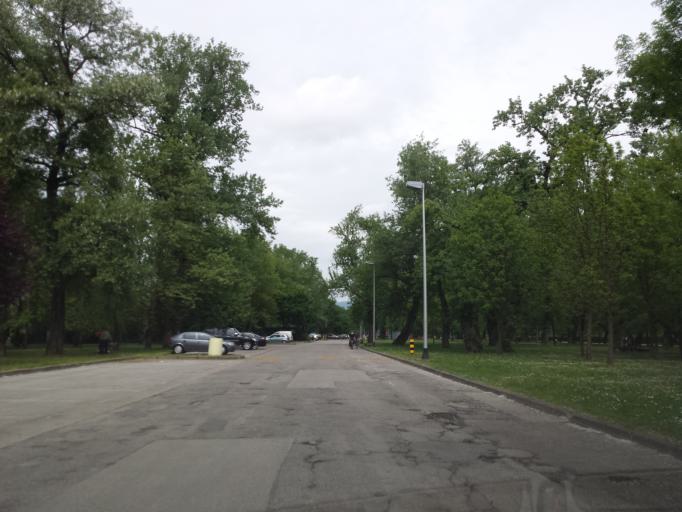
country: HR
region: Grad Zagreb
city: Jankomir
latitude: 45.7773
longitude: 15.9379
